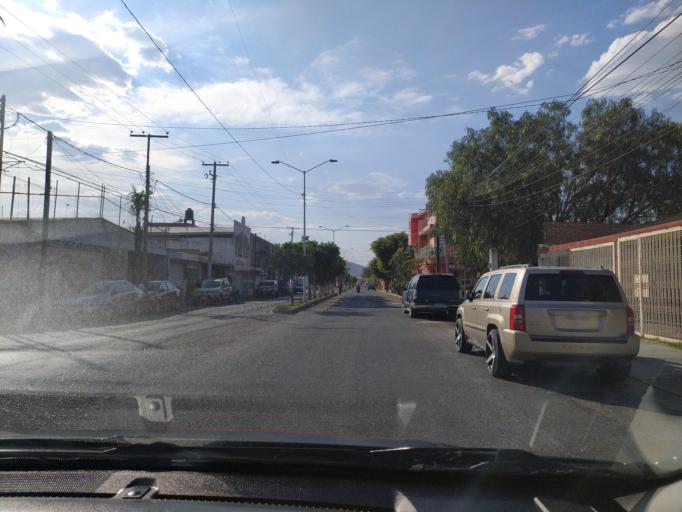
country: MX
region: Guanajuato
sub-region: San Francisco del Rincon
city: Fraccionamiento la Mezquitera
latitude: 21.0126
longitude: -101.8407
